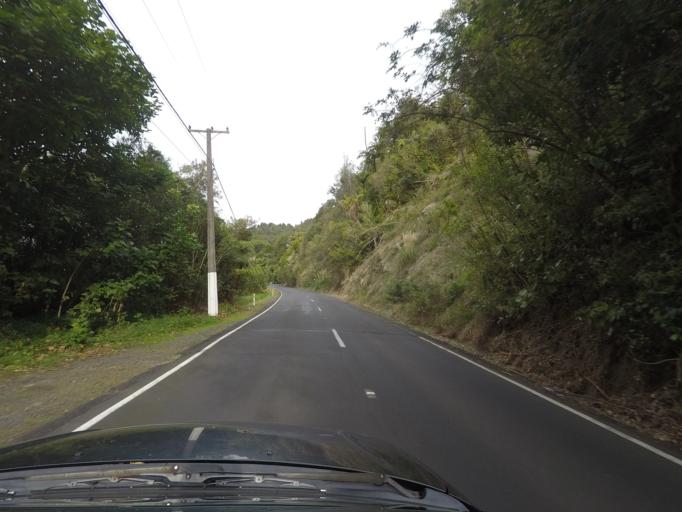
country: NZ
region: Auckland
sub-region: Auckland
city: Titirangi
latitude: -36.9362
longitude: 174.5792
